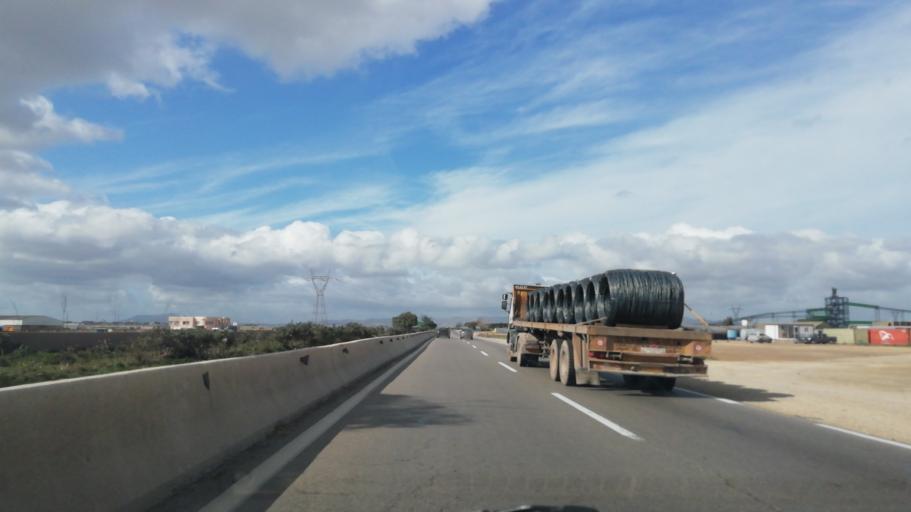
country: DZ
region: Oran
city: Ain el Bya
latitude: 35.7762
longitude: -0.2574
